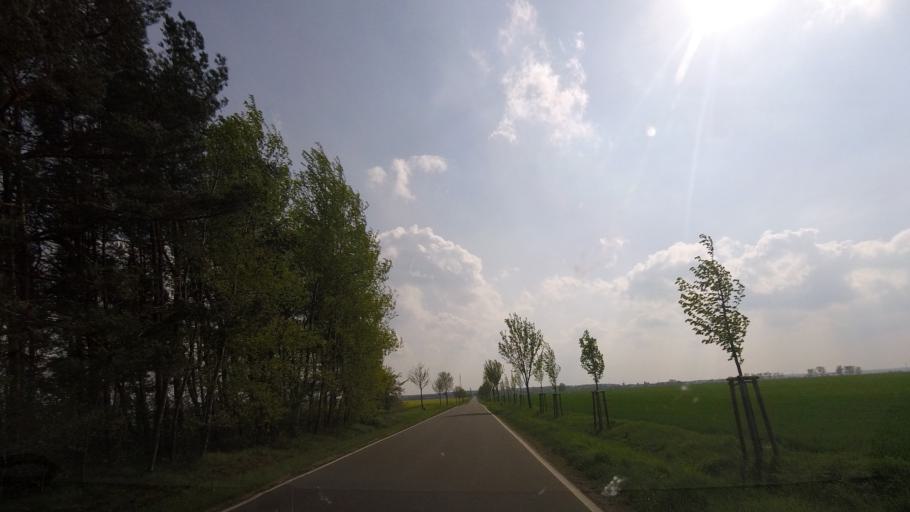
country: DE
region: Saxony-Anhalt
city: Zahna
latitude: 51.9586
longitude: 12.8485
